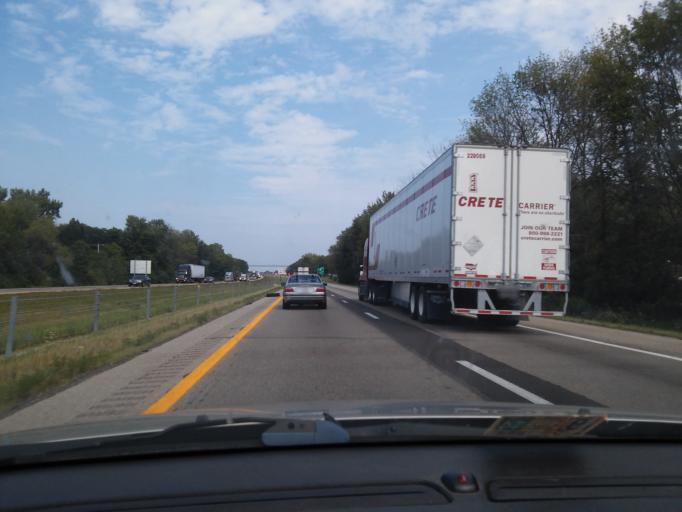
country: US
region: Ohio
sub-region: Montgomery County
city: Englewood
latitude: 39.8550
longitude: -84.3052
